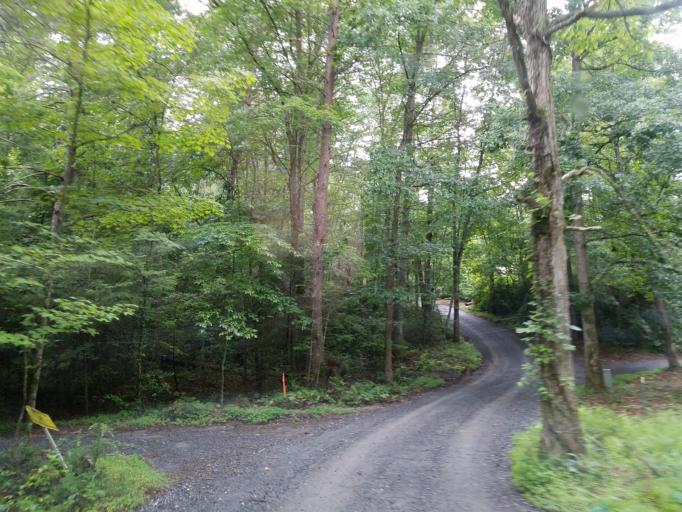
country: US
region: Georgia
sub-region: Fannin County
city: Blue Ridge
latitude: 34.7975
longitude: -84.2858
